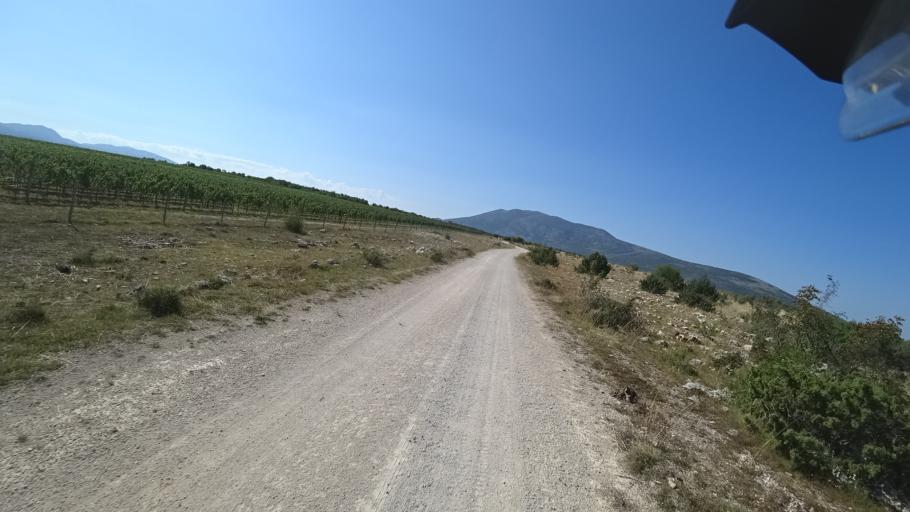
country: HR
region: Sibensko-Kniniska
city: Knin
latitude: 43.9916
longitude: 16.1928
